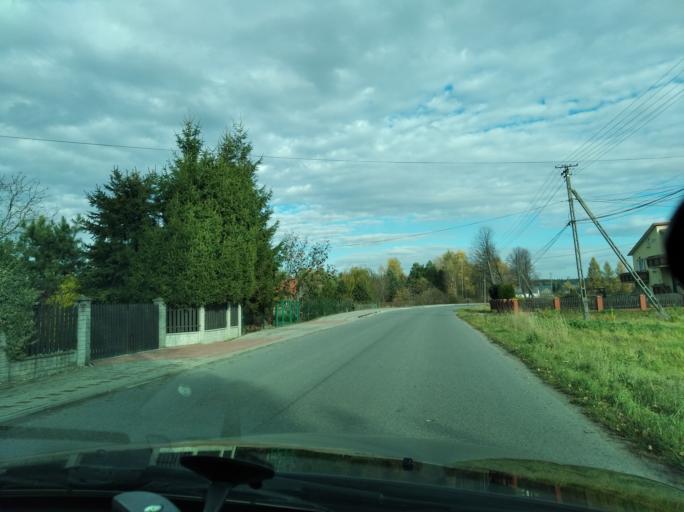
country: PL
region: Subcarpathian Voivodeship
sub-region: Powiat debicki
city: Brzeznica
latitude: 50.0935
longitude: 21.5314
